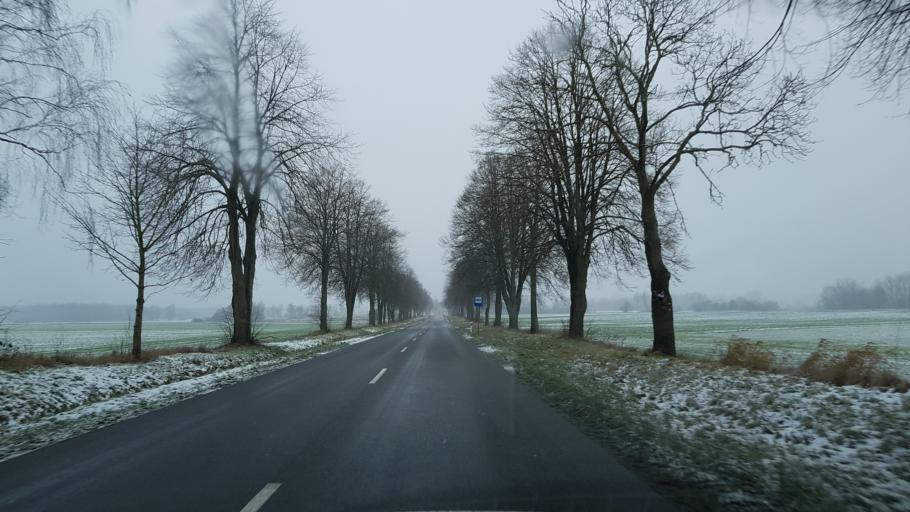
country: PL
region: West Pomeranian Voivodeship
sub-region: Powiat gryficki
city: Gryfice
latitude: 53.9427
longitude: 15.1407
